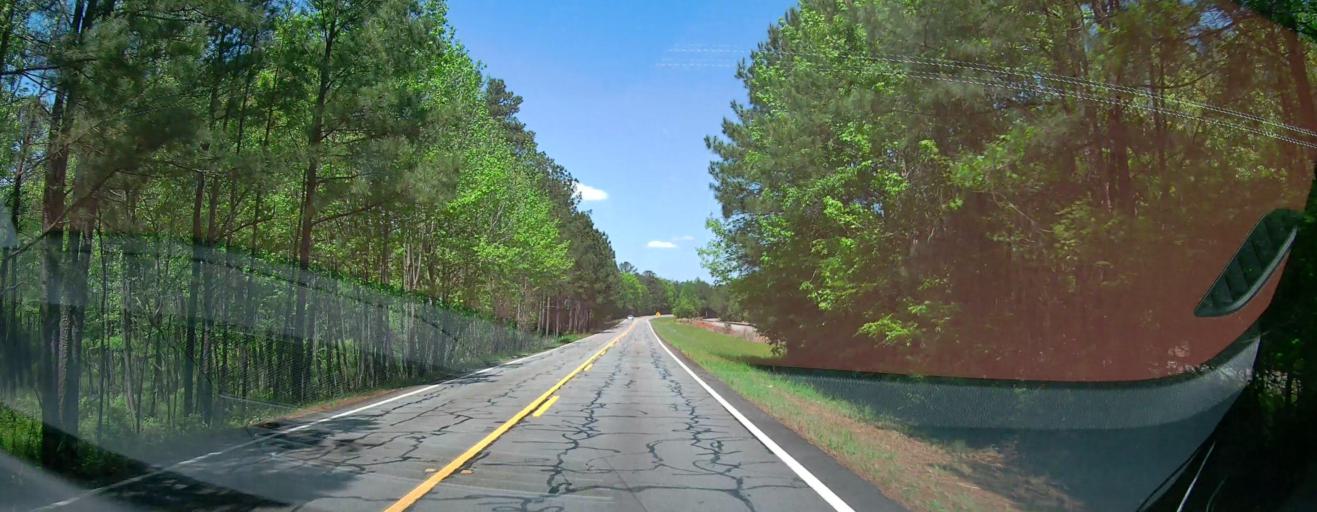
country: US
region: Georgia
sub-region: Jones County
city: Gray
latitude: 33.1384
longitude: -83.6329
